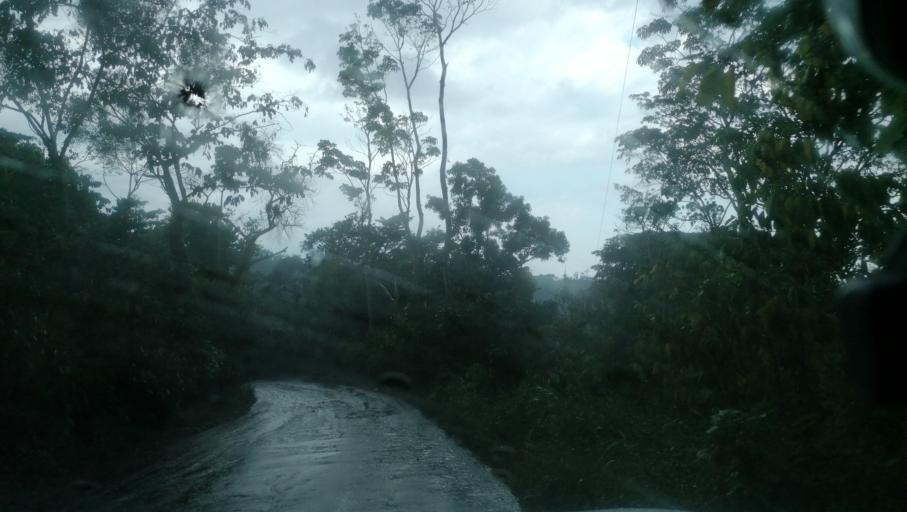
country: MX
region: Chiapas
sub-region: Cacahoatan
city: Benito Juarez
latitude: 15.0689
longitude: -92.1912
